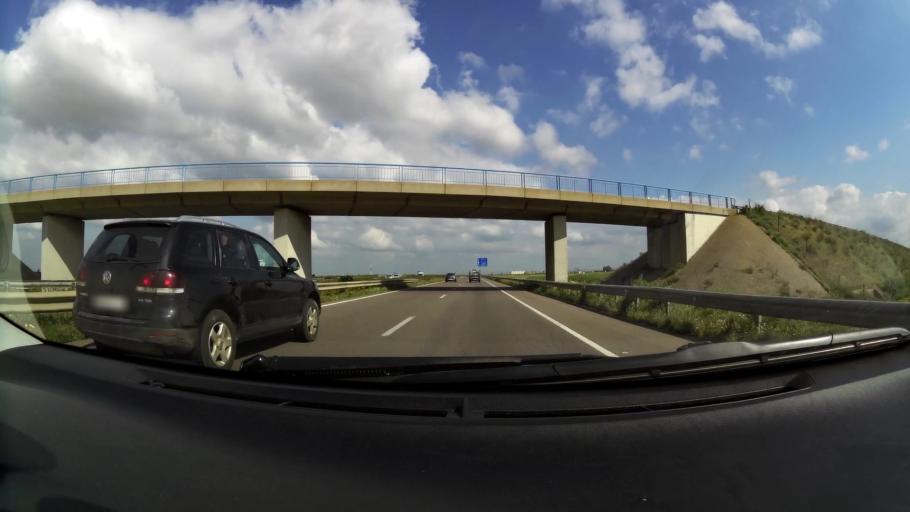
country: MA
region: Chaouia-Ouardigha
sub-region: Settat Province
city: Berrechid
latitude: 33.3063
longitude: -7.5848
